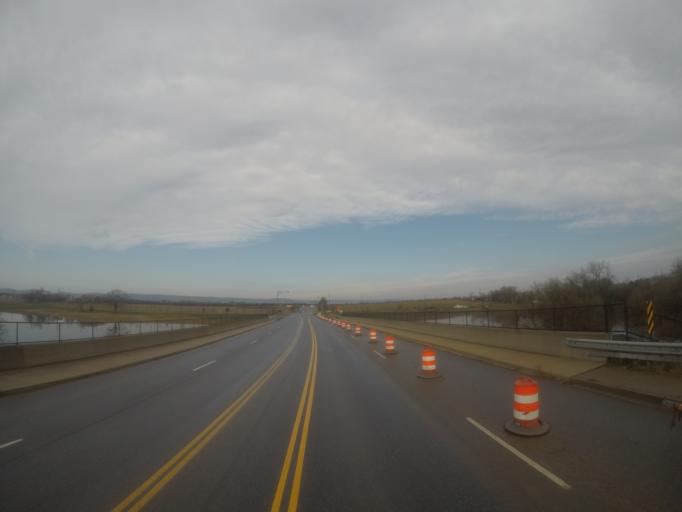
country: US
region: Maryland
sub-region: Frederick County
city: Frederick
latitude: 39.4246
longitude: -77.3840
